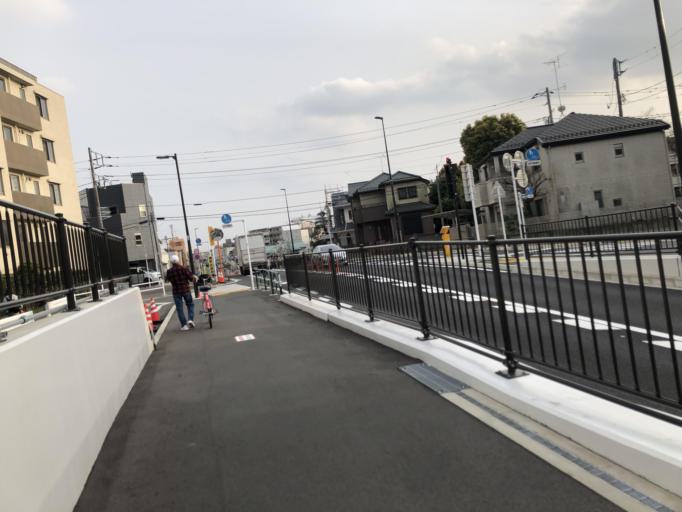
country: JP
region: Tokyo
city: Tokyo
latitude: 35.6444
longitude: 139.6423
